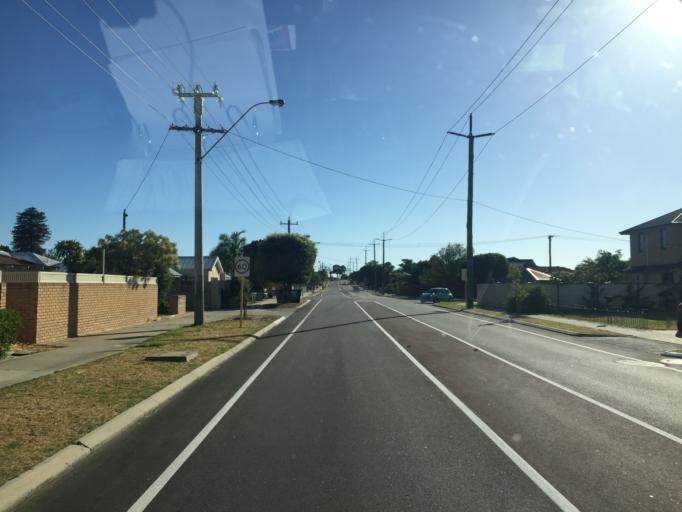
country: AU
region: Western Australia
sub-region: Belmont
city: Rivervale
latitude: -31.9651
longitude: 115.9236
